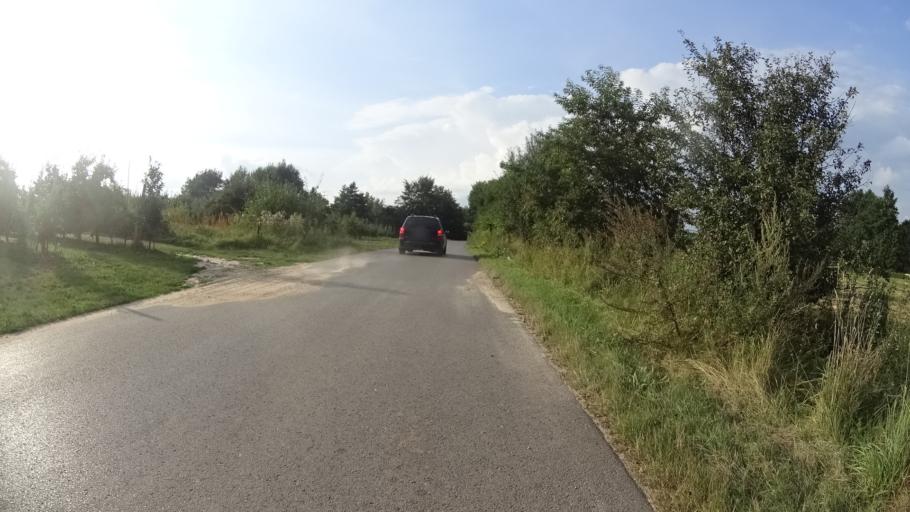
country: PL
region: Masovian Voivodeship
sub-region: Powiat grojecki
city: Mogielnica
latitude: 51.6810
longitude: 20.7327
